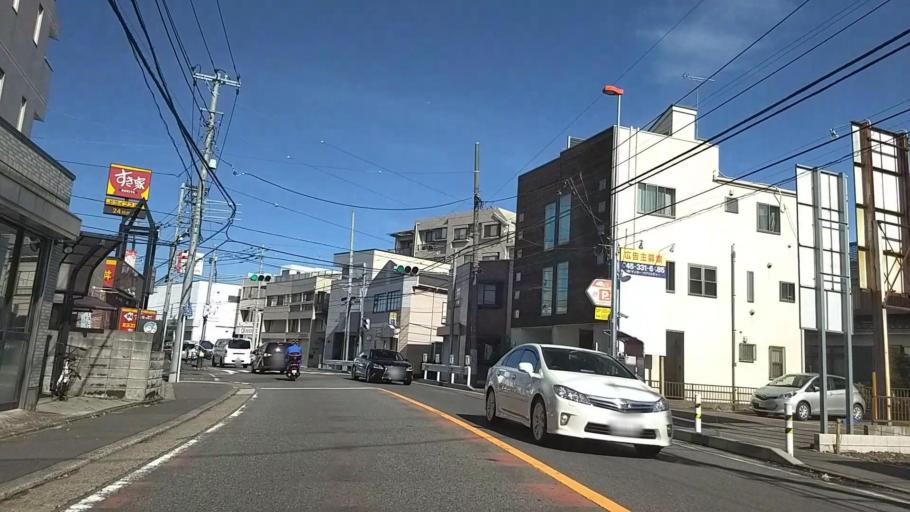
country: JP
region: Kanagawa
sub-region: Kawasaki-shi
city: Kawasaki
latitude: 35.5623
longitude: 139.6494
